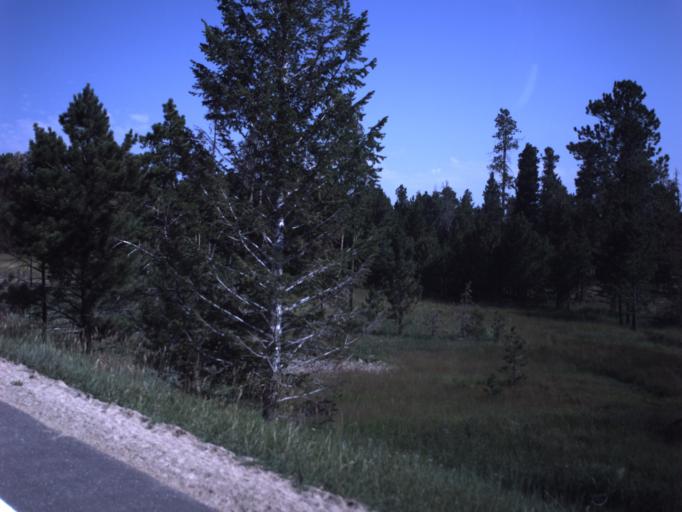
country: US
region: Utah
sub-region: Daggett County
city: Manila
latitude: 40.8521
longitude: -109.5903
